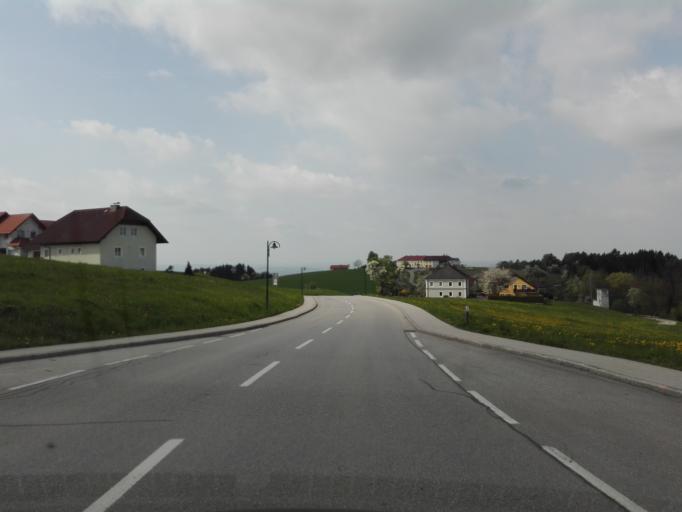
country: AT
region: Upper Austria
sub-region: Politischer Bezirk Perg
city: Perg
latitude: 48.2814
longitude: 14.6777
